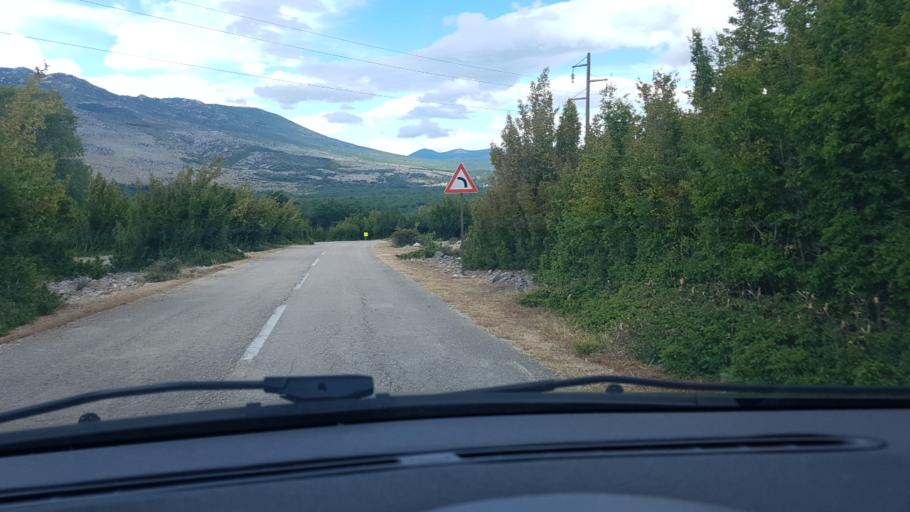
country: HR
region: Zadarska
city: Gracac
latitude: 44.1845
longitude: 15.8965
